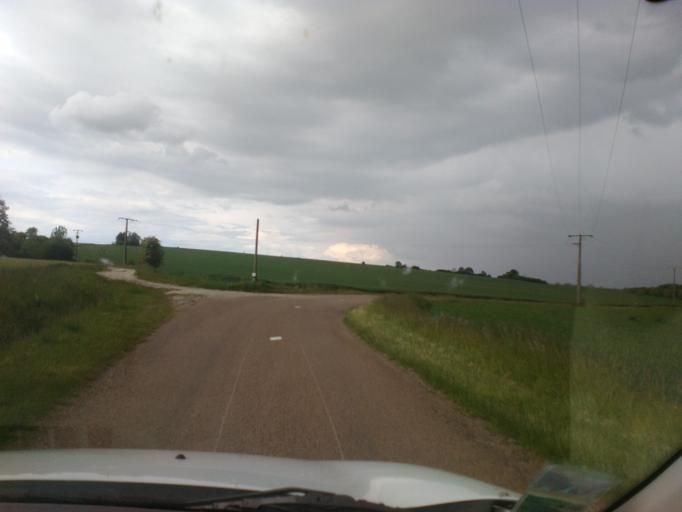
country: FR
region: Champagne-Ardenne
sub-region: Departement de l'Aube
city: Nogent-sur-Seine
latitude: 48.3843
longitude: 3.5141
